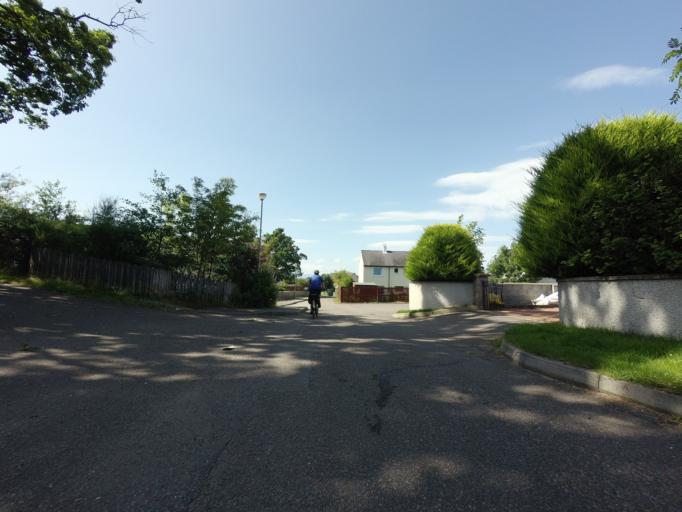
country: GB
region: Scotland
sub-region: Highland
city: Inverness
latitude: 57.4829
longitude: -4.1480
